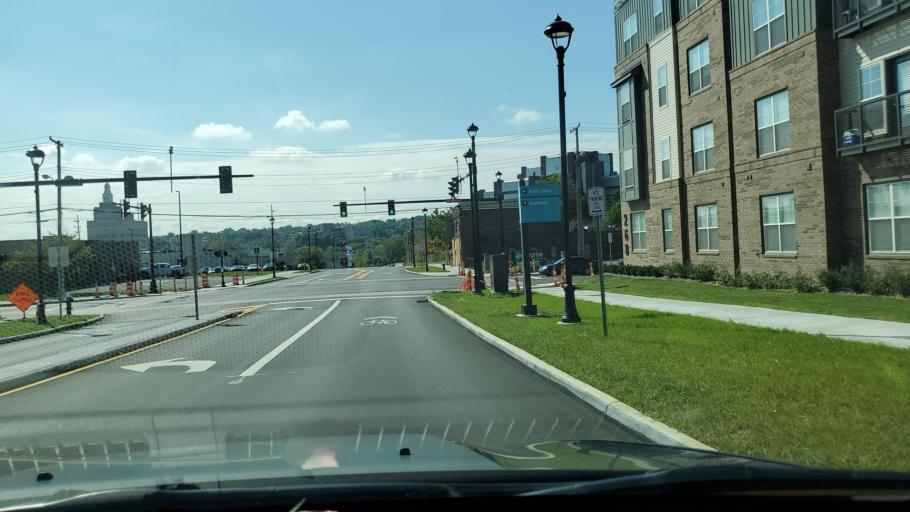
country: US
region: Ohio
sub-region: Mahoning County
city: Youngstown
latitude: 41.1058
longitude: -80.6528
